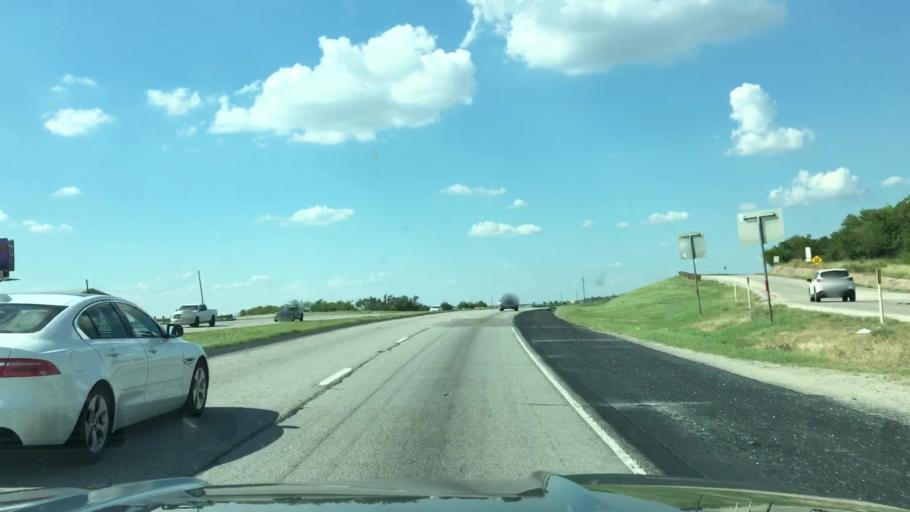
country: US
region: Texas
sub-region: Wise County
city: Rhome
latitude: 33.0517
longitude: -97.4785
